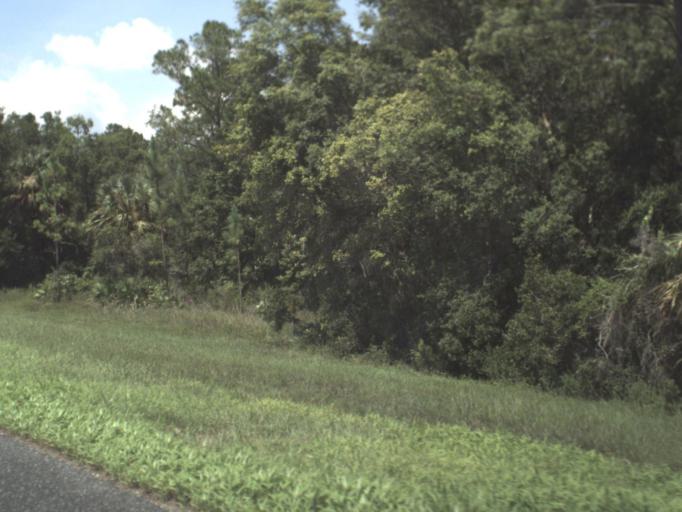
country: US
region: Florida
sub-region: Levy County
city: Inglis
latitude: 29.1339
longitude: -82.6370
